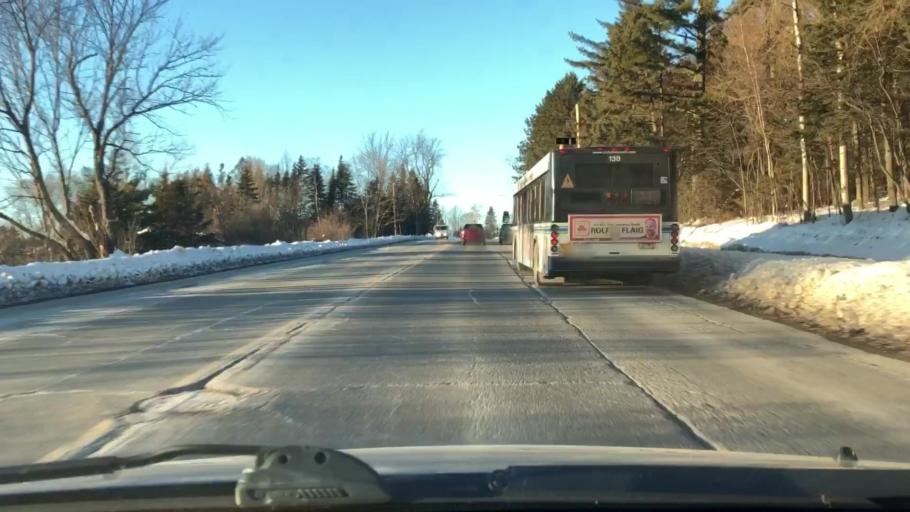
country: US
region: Minnesota
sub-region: Saint Louis County
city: Arnold
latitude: 46.8415
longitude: -92.0827
